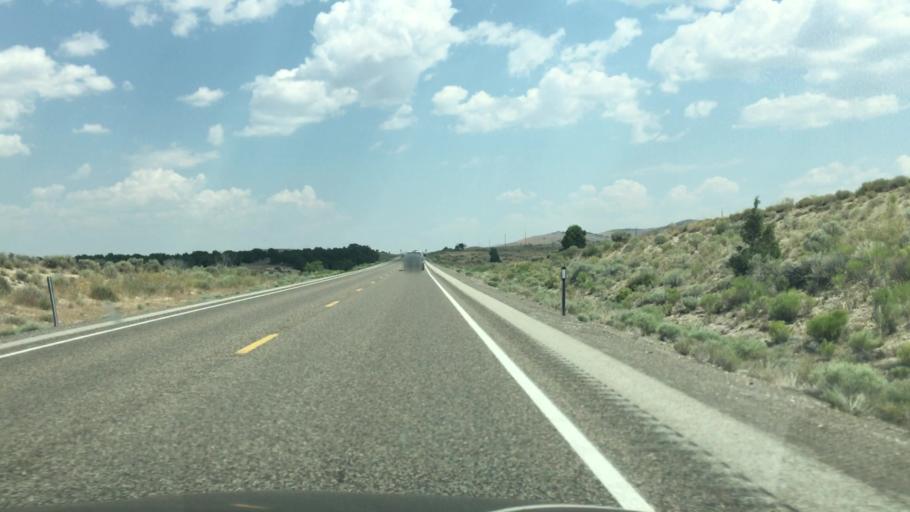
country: US
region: Nevada
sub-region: Elko County
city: Wells
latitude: 41.2001
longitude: -114.8600
